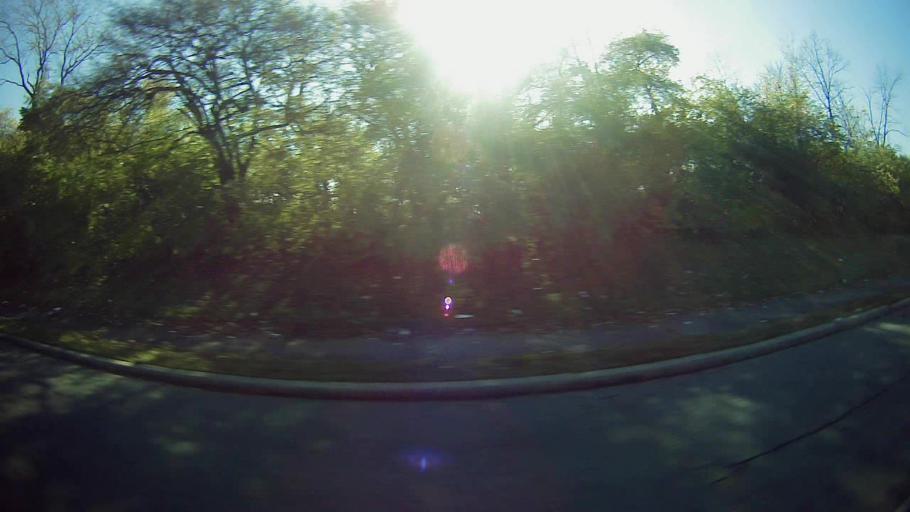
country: US
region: Michigan
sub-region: Wayne County
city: Dearborn Heights
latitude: 42.3571
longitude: -83.2646
